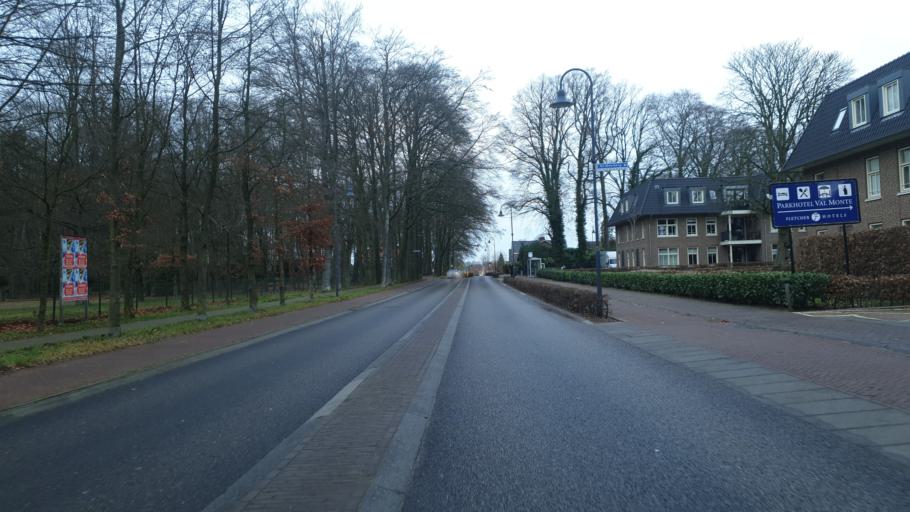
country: NL
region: Gelderland
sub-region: Gemeente Groesbeek
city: Berg en Dal
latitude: 51.8230
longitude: 5.9155
